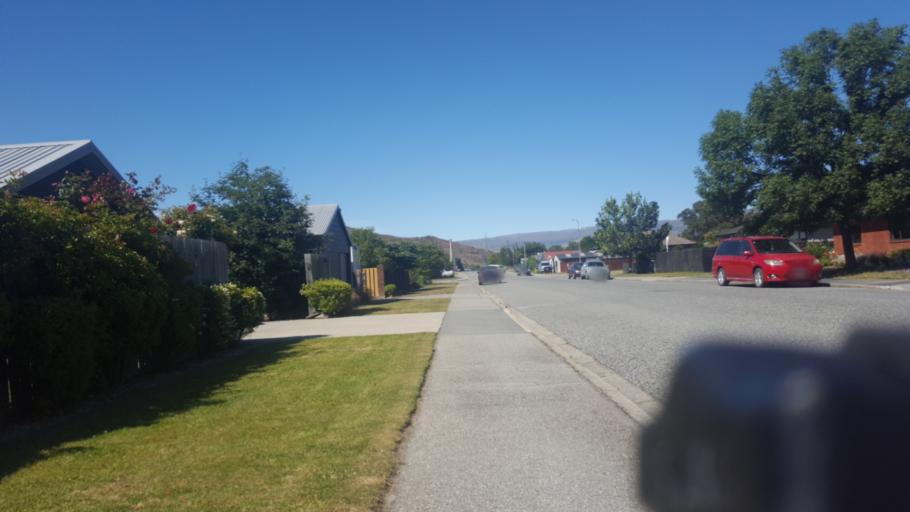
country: NZ
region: Otago
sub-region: Queenstown-Lakes District
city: Wanaka
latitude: -45.0451
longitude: 169.2069
